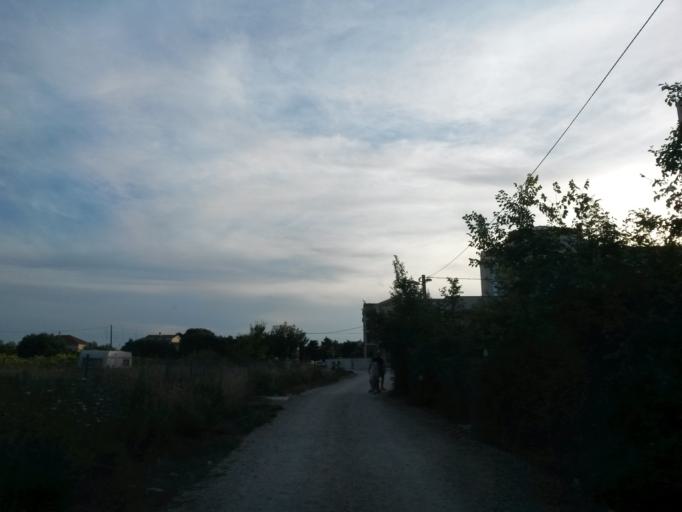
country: HR
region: Splitsko-Dalmatinska
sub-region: Grad Trogir
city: Trogir
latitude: 43.5432
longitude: 16.3200
